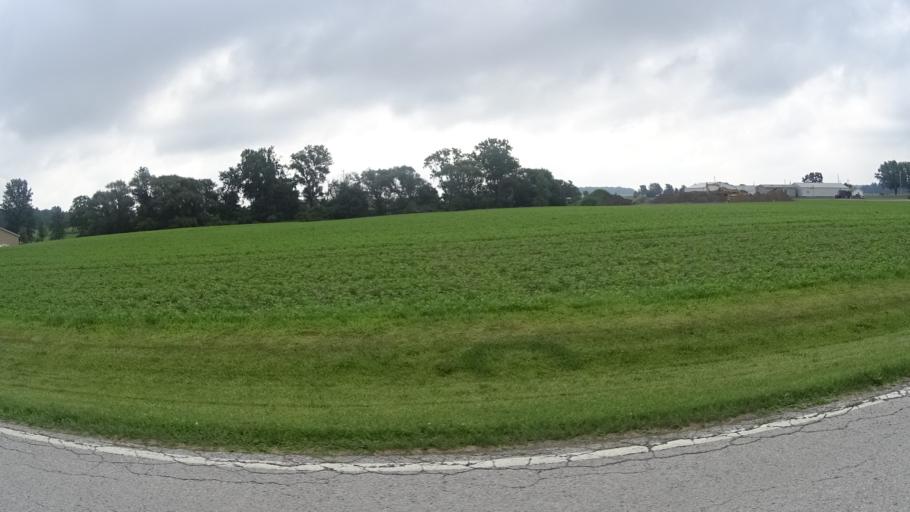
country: US
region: Ohio
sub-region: Erie County
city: Milan
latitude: 41.2819
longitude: -82.5083
